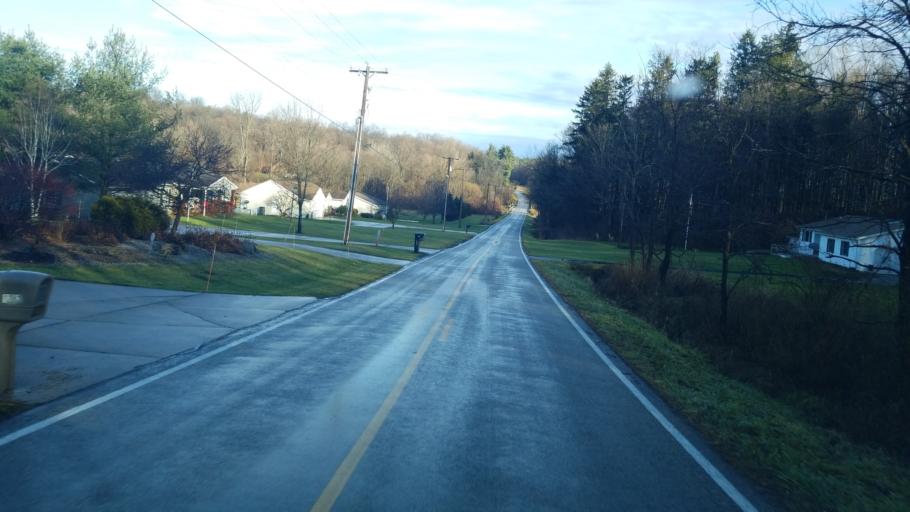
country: US
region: Ohio
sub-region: Richland County
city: Mansfield
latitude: 40.7212
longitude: -82.4894
